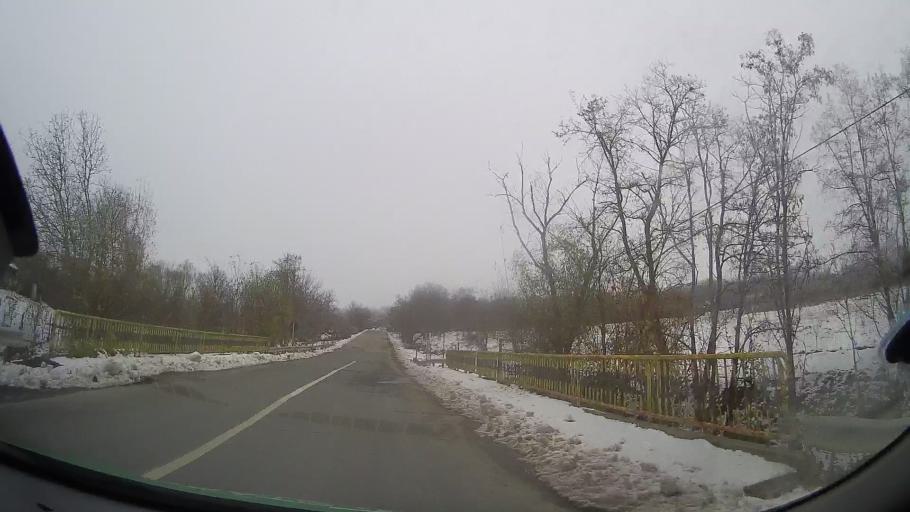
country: RO
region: Vrancea
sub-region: Comuna Boghesti
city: Boghesti
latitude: 46.2043
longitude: 27.4407
